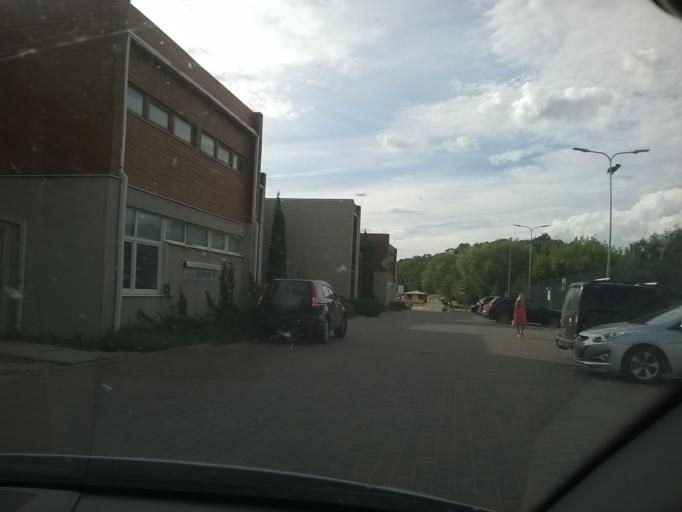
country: EE
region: Vorumaa
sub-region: Voru linn
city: Voru
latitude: 57.8431
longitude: 26.9933
